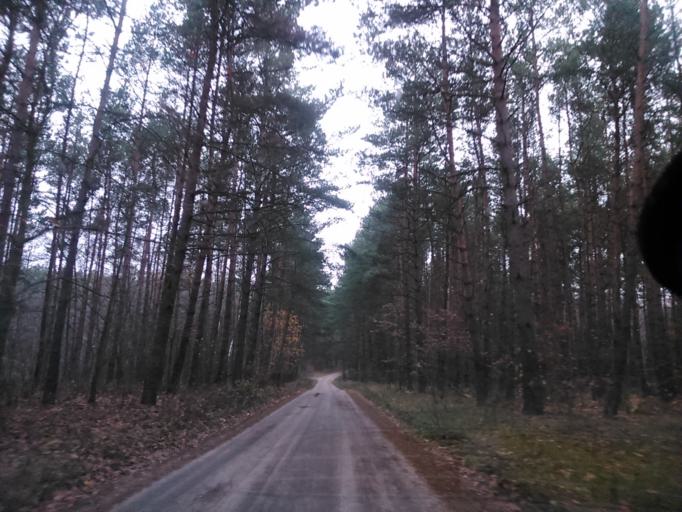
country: PL
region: Kujawsko-Pomorskie
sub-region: Powiat golubsko-dobrzynski
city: Golub-Dobrzyn
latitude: 53.1107
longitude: 19.0973
